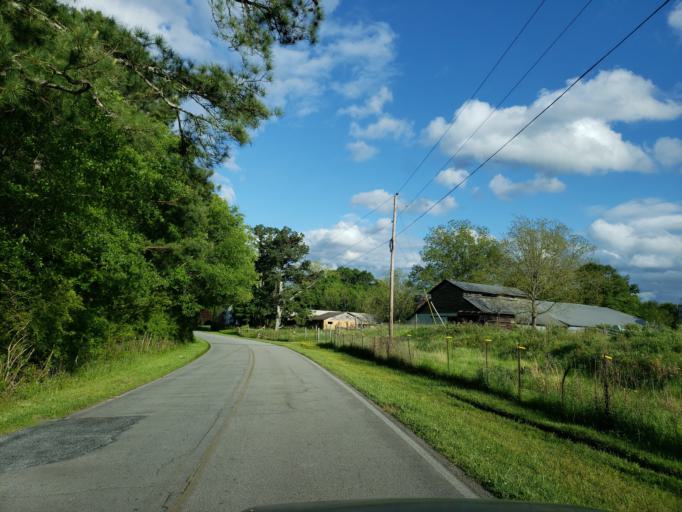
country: US
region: Georgia
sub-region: Haralson County
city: Tallapoosa
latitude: 33.7730
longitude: -85.3041
